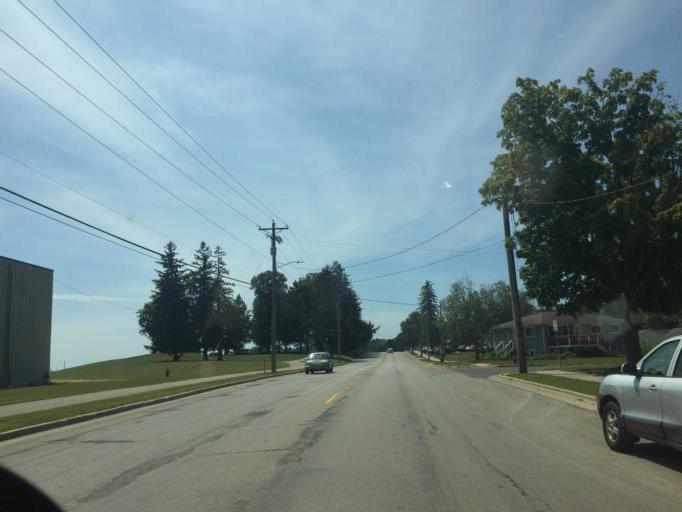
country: US
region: Minnesota
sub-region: Olmsted County
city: Rochester
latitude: 43.9920
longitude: -92.4592
